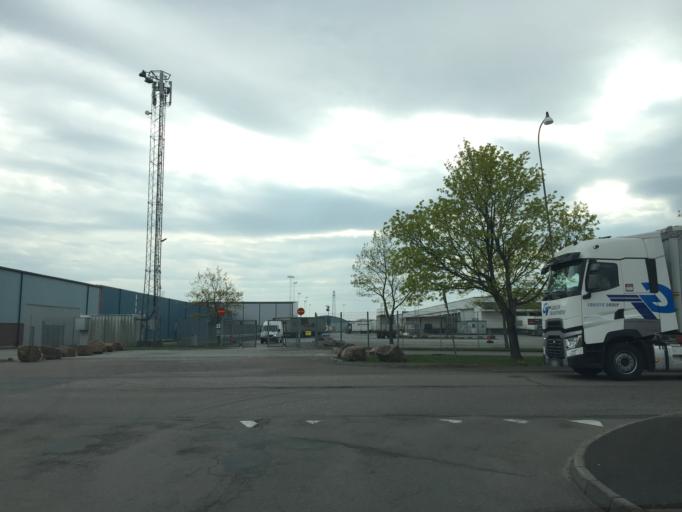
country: SE
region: Vaestra Goetaland
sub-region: Goteborg
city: Hammarkullen
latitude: 57.7677
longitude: 11.9992
